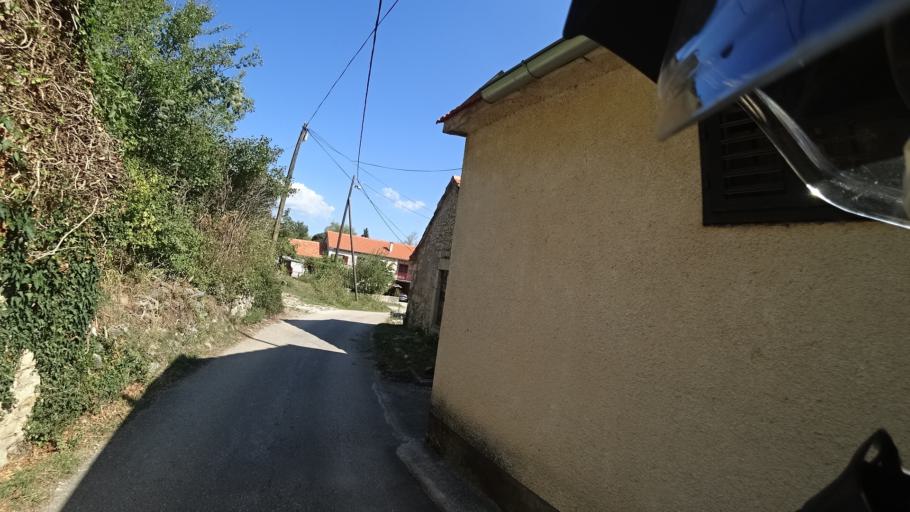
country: HR
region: Sibensko-Kniniska
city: Drnis
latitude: 43.8776
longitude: 16.1885
